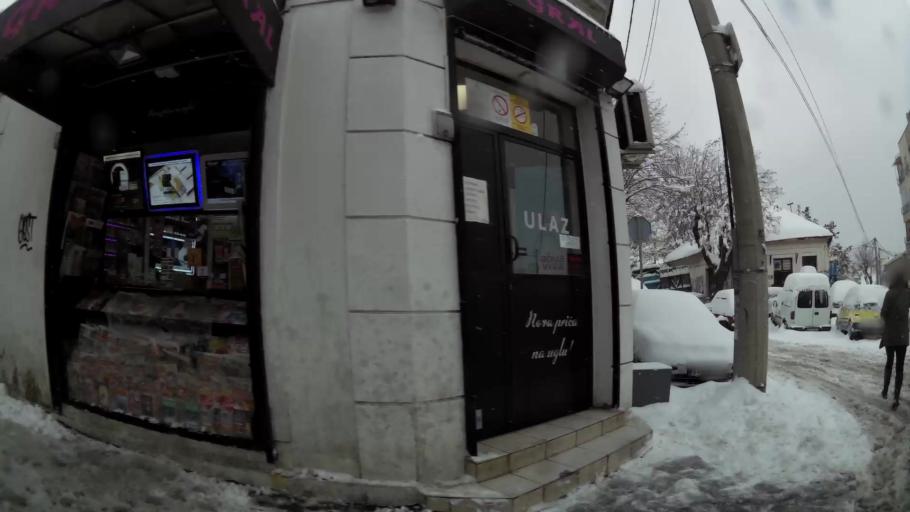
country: RS
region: Central Serbia
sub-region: Belgrade
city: Vracar
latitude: 44.7897
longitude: 20.4802
